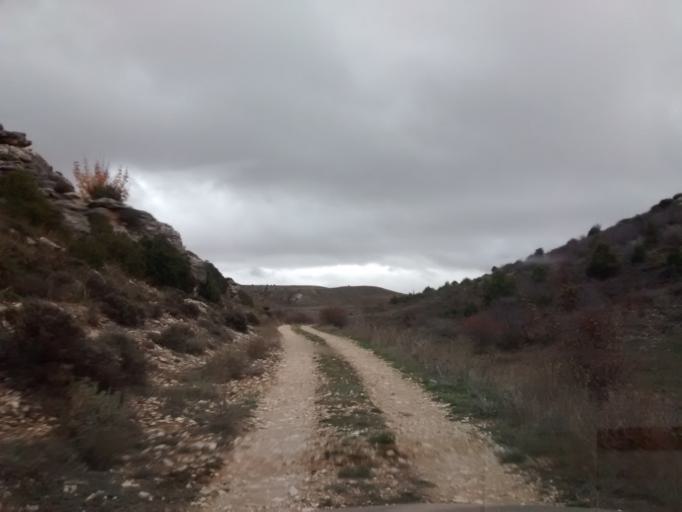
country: ES
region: Aragon
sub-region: Provincia de Zaragoza
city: Torralba de los Frailes
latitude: 41.0286
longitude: -1.6851
